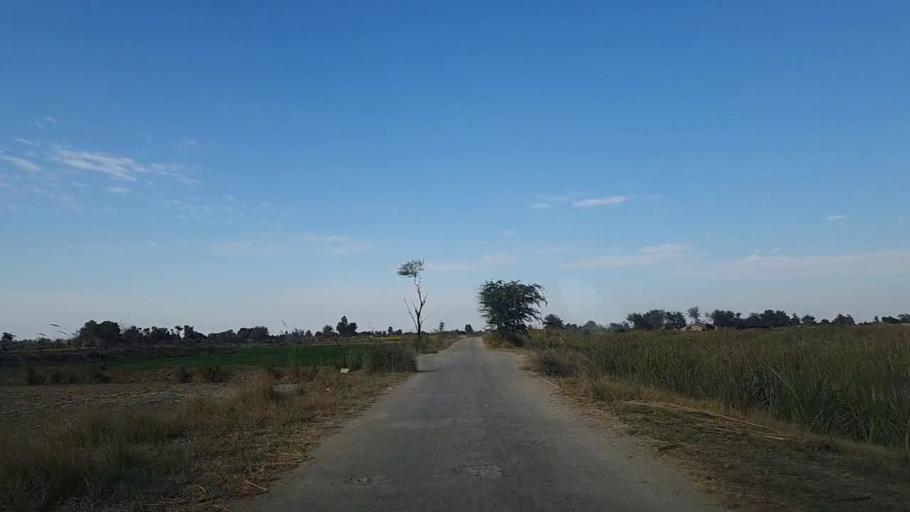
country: PK
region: Sindh
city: Khadro
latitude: 26.2843
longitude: 68.8199
